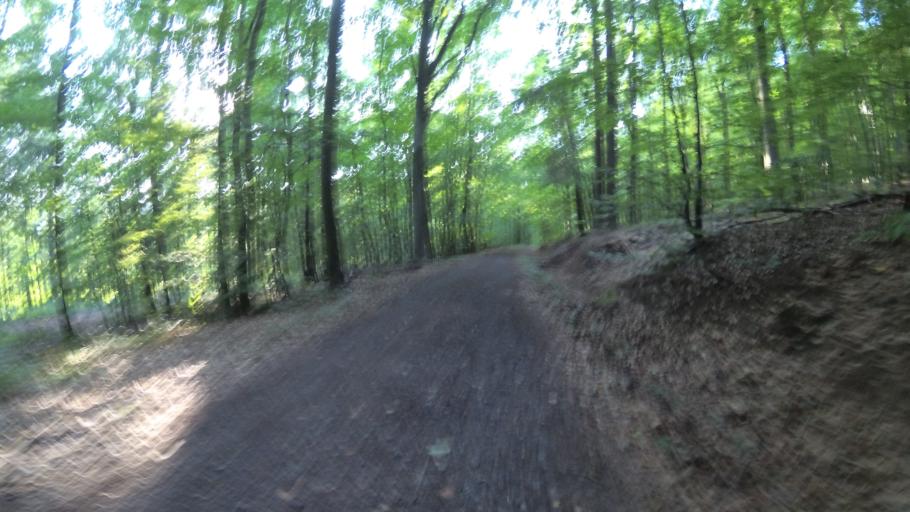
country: DE
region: Saarland
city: Sankt Wendel
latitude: 49.4428
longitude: 7.1505
